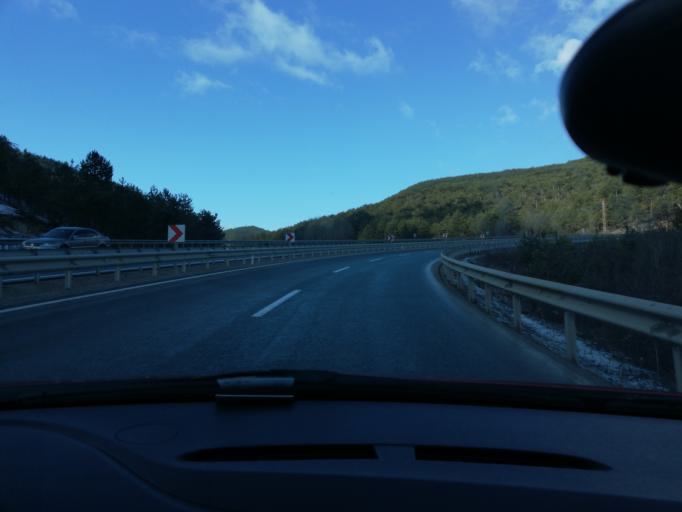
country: TR
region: Kastamonu
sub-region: Cide
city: Kastamonu
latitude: 41.3610
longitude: 33.7556
